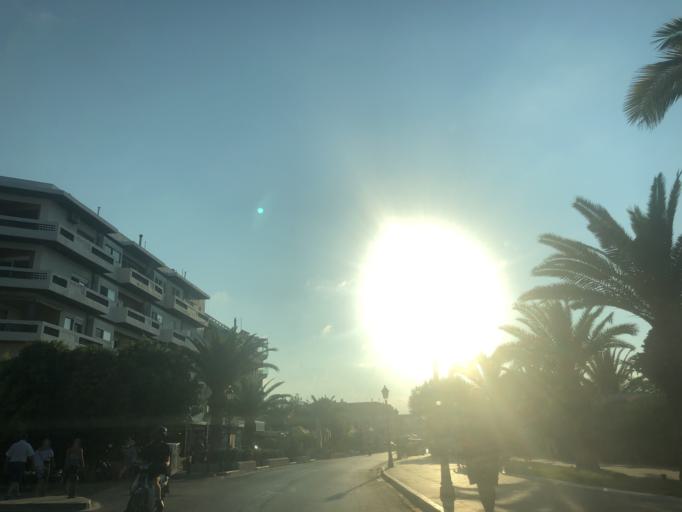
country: GR
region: Crete
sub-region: Nomos Rethymnis
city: Rethymno
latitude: 35.3667
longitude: 24.4815
